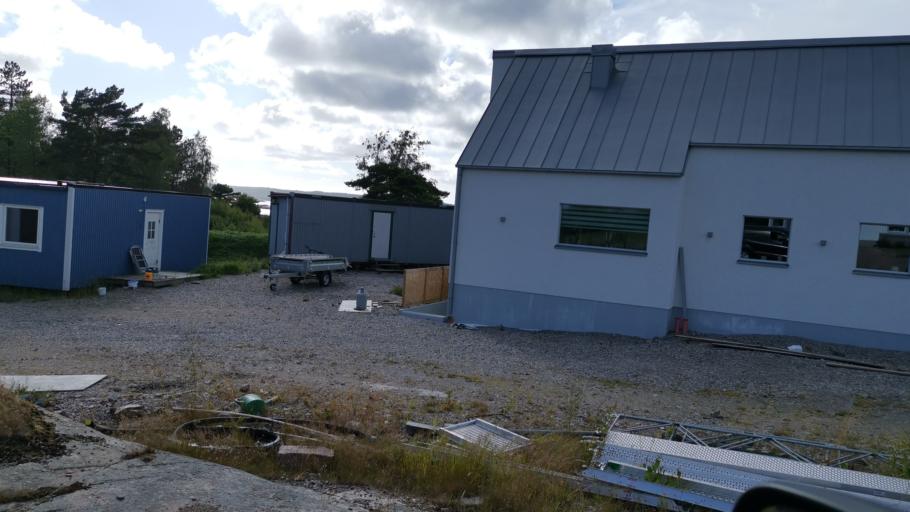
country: SE
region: Vaestra Goetaland
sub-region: Tjorns Kommun
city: Myggenas
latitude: 58.1040
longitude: 11.6387
